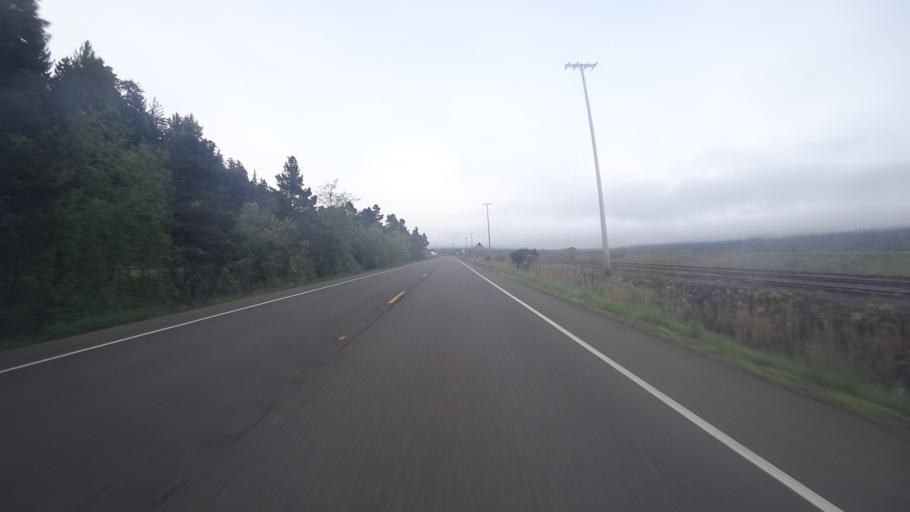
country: US
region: Oregon
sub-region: Douglas County
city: Reedsport
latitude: 43.7369
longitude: -124.1112
